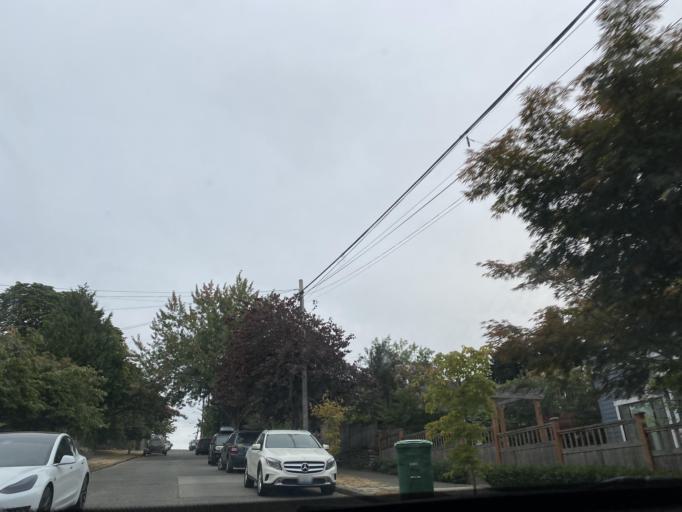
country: US
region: Washington
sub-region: King County
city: Seattle
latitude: 47.6518
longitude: -122.3716
